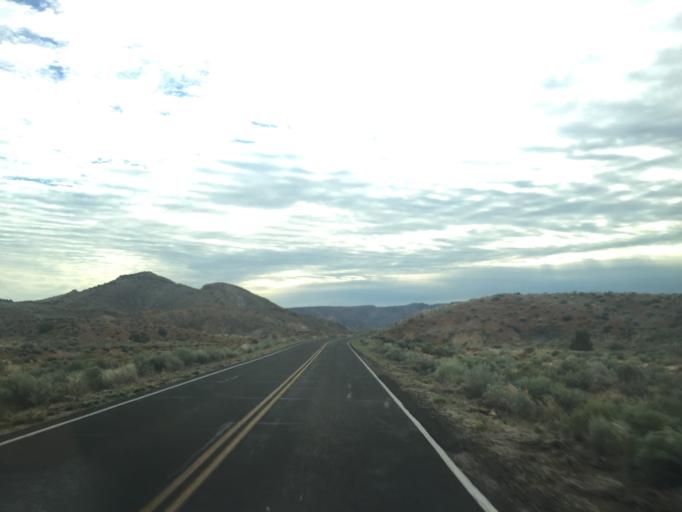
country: US
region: Utah
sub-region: Grand County
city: Moab
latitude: 38.7325
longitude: -109.5531
